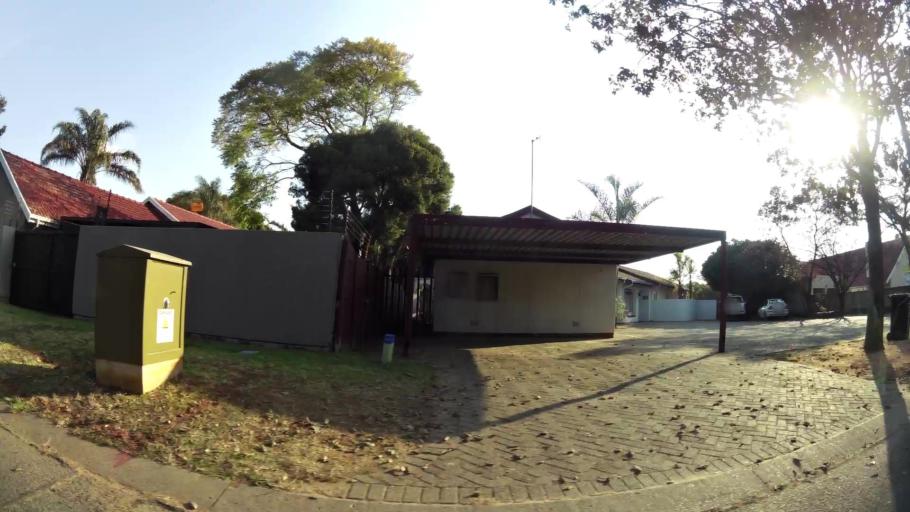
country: ZA
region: Gauteng
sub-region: City of Johannesburg Metropolitan Municipality
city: Modderfontein
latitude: -26.0735
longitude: 28.2147
